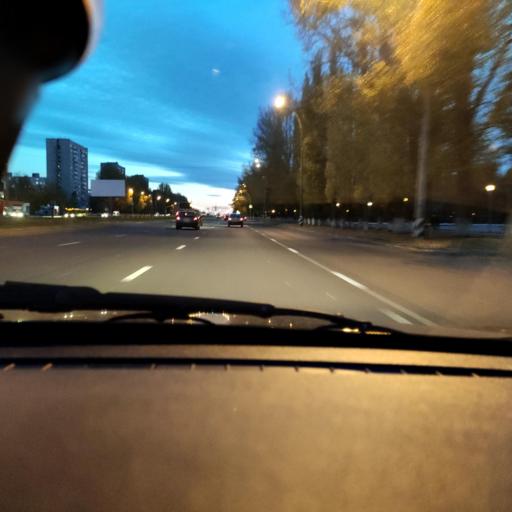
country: RU
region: Samara
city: Tol'yatti
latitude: 53.5109
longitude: 49.2769
